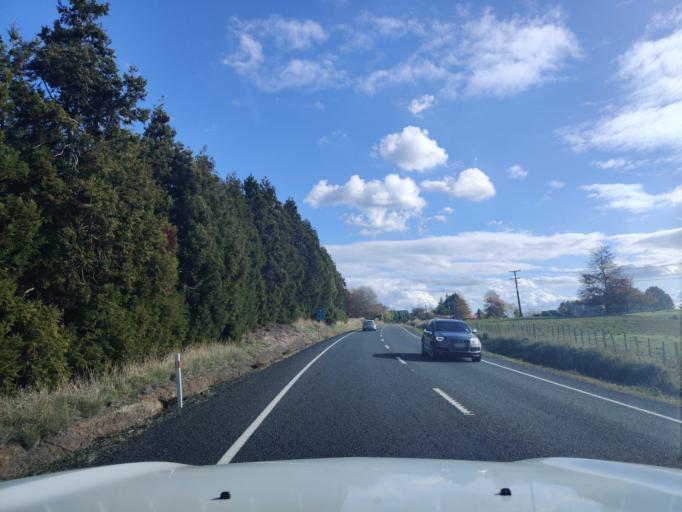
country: NZ
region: Waikato
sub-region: Hauraki District
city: Ngatea
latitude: -37.2897
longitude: 175.3839
